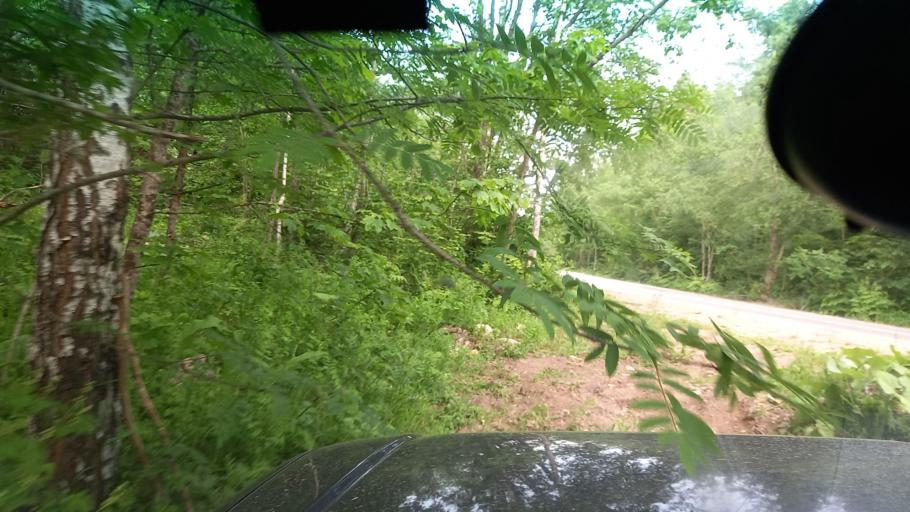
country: RU
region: Adygeya
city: Kamennomostskiy
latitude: 44.1514
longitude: 40.0640
